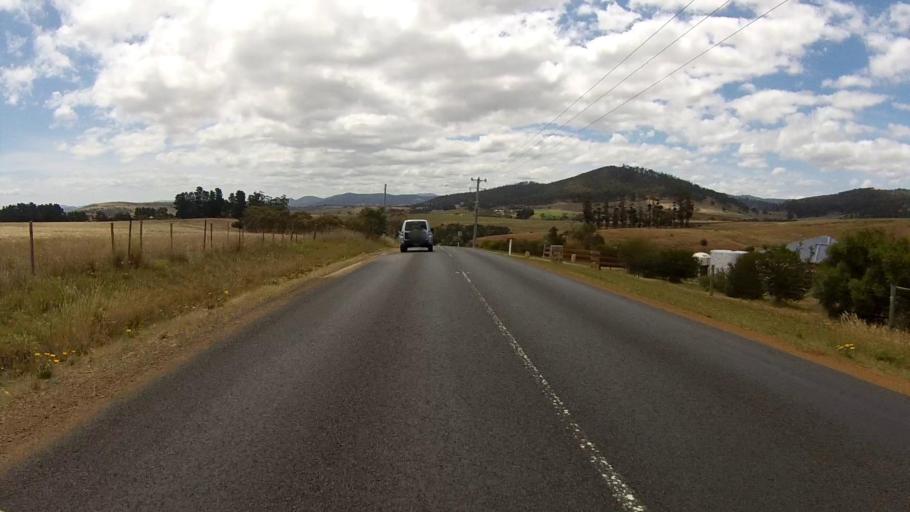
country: AU
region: Tasmania
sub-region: Sorell
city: Sorell
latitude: -42.8113
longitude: 147.6131
